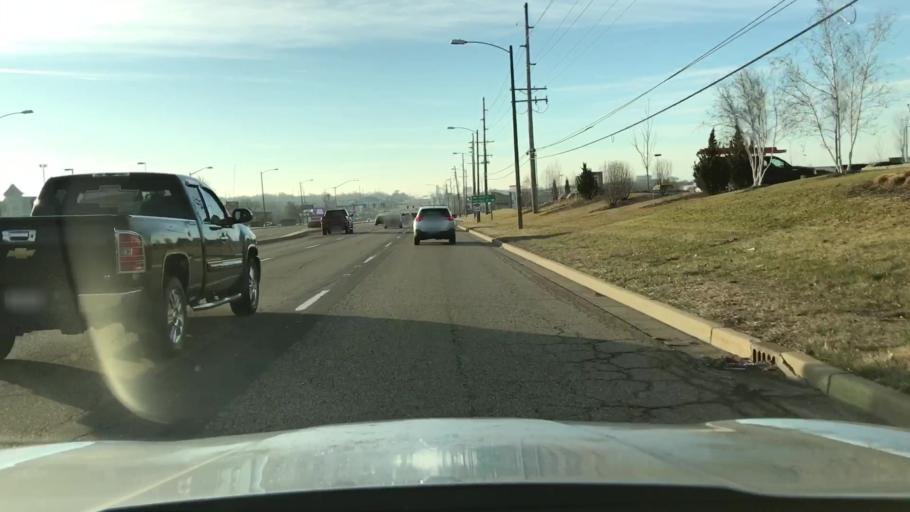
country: US
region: Illinois
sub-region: McLean County
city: Normal
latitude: 40.5095
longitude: -88.9535
